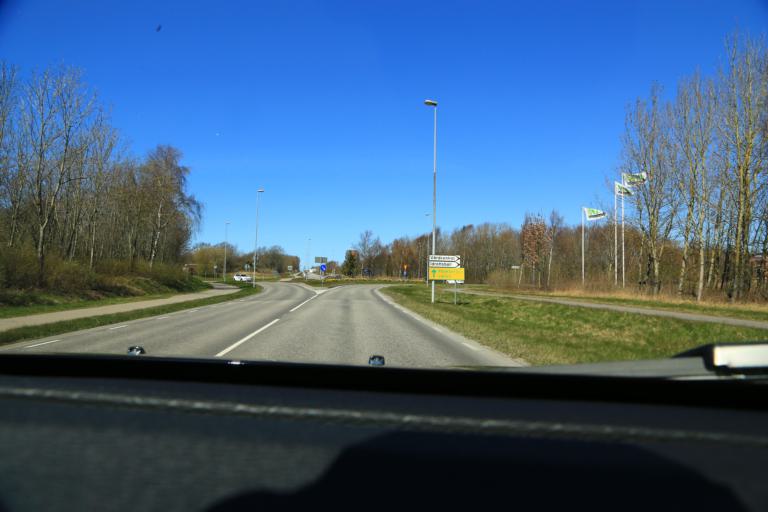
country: SE
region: Halland
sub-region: Varbergs Kommun
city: Traslovslage
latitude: 57.0843
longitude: 12.2737
